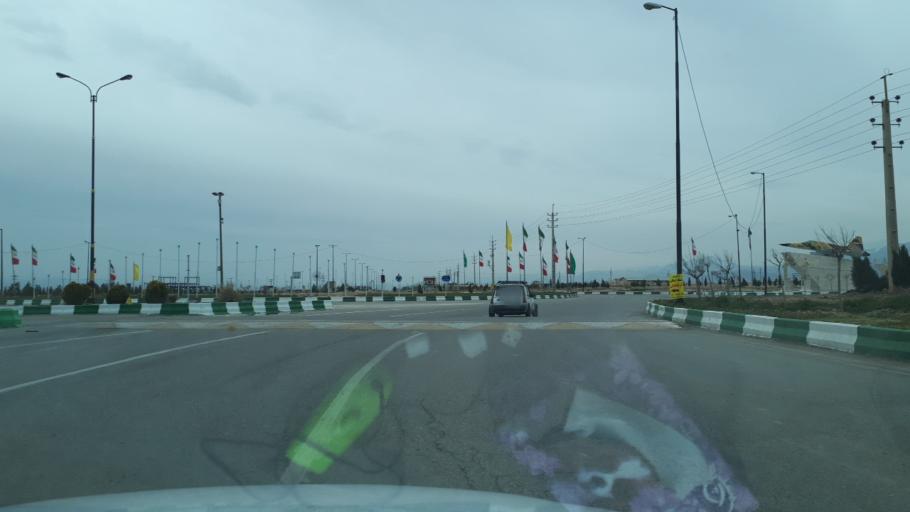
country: IR
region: Semnan
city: Damghan
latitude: 36.1449
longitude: 54.3171
